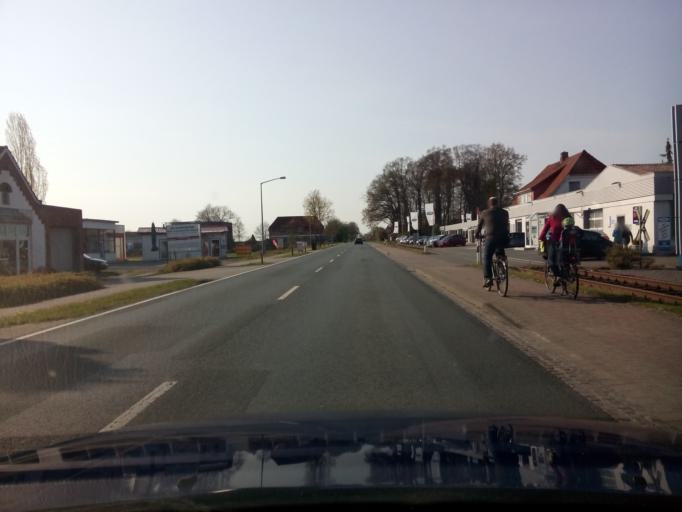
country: DE
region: Lower Saxony
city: Syke
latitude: 52.8807
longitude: 8.8622
